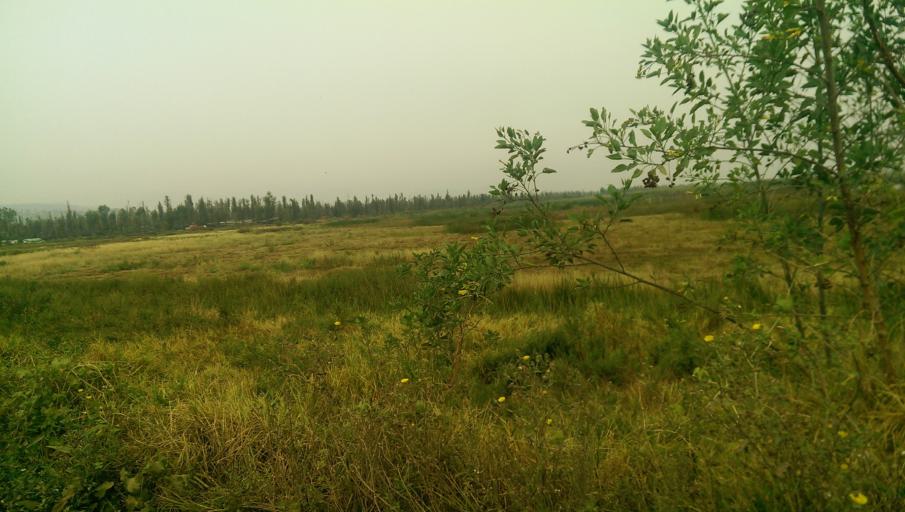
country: MX
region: Mexico City
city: Tlahuac
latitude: 19.2649
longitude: -99.0463
